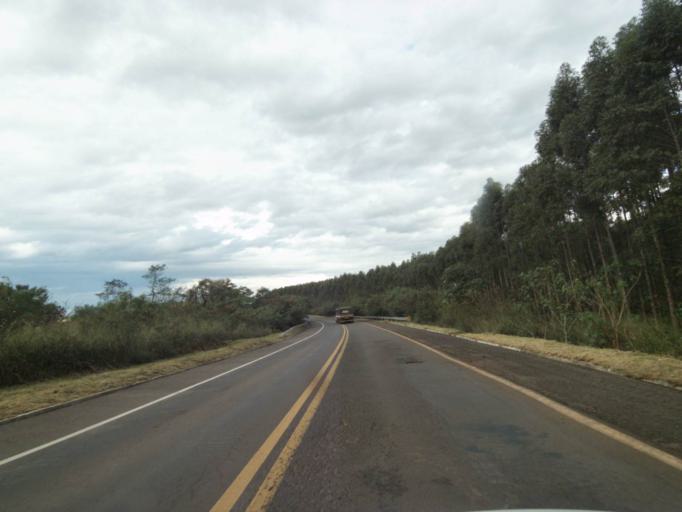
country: PY
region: Canindeyu
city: Salto del Guaira
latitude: -24.0850
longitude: -54.0832
